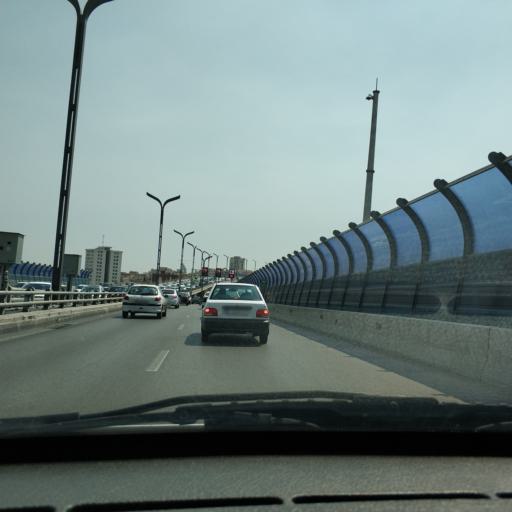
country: IR
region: Tehran
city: Tajrish
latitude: 35.7826
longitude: 51.4343
